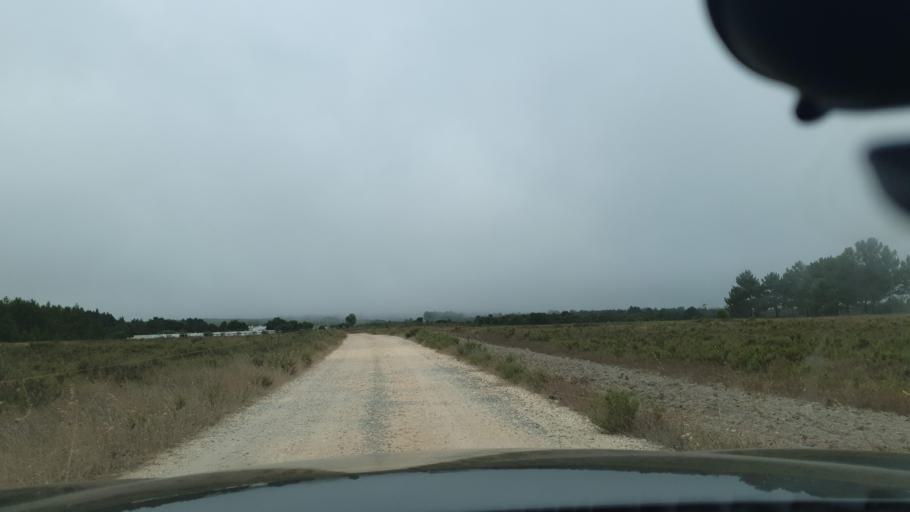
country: PT
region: Beja
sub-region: Odemira
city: Sao Teotonio
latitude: 37.4960
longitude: -8.6833
